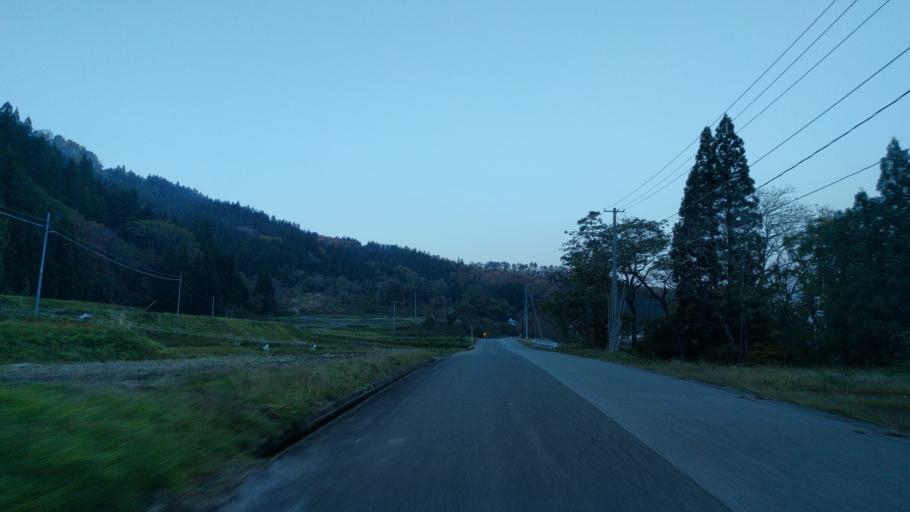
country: JP
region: Fukushima
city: Kitakata
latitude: 37.5166
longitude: 139.7048
